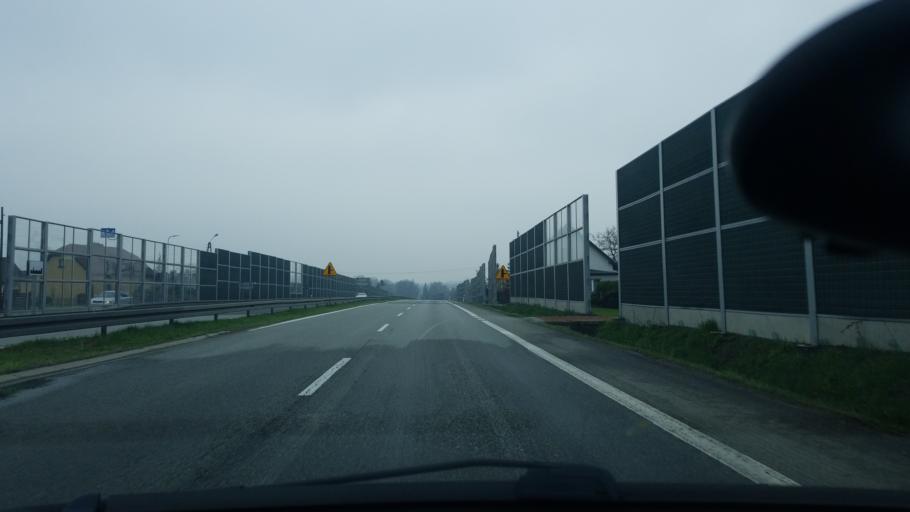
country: PL
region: Silesian Voivodeship
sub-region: Powiat pszczynski
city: Pawlowice
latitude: 49.9732
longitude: 18.7168
